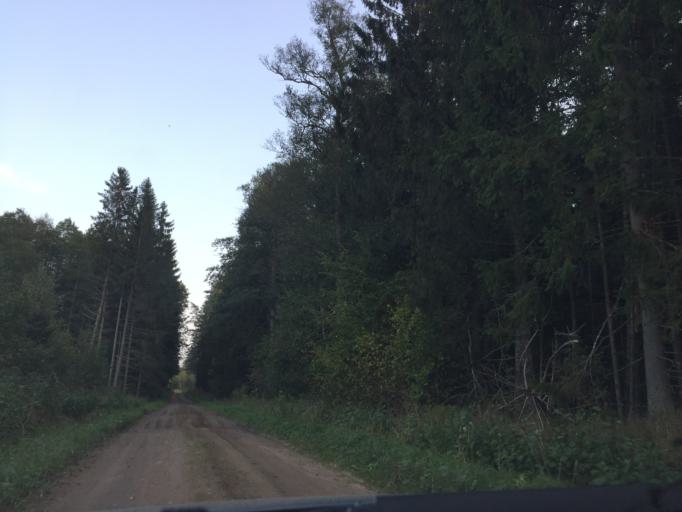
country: LV
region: Ikskile
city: Ikskile
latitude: 56.9302
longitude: 24.4904
